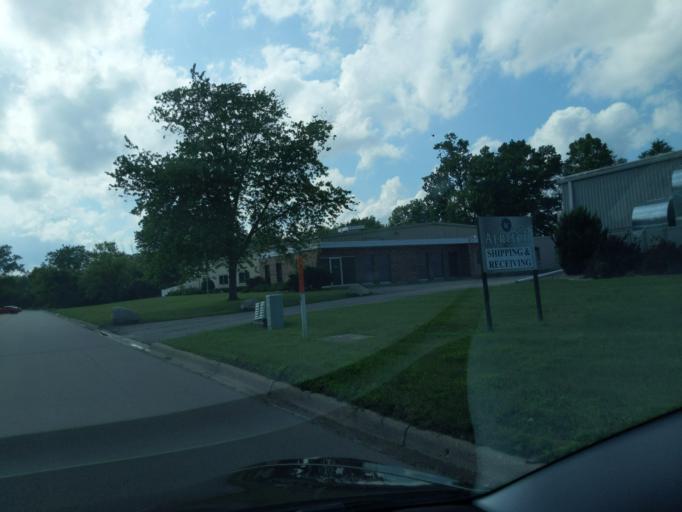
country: US
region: Michigan
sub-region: Jackson County
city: Jackson
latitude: 42.2262
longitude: -84.3670
